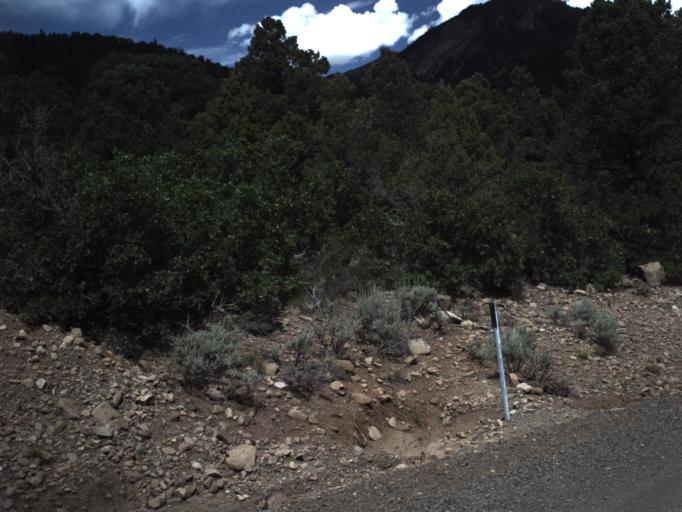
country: US
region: Utah
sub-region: Piute County
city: Junction
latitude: 38.2618
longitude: -112.3065
